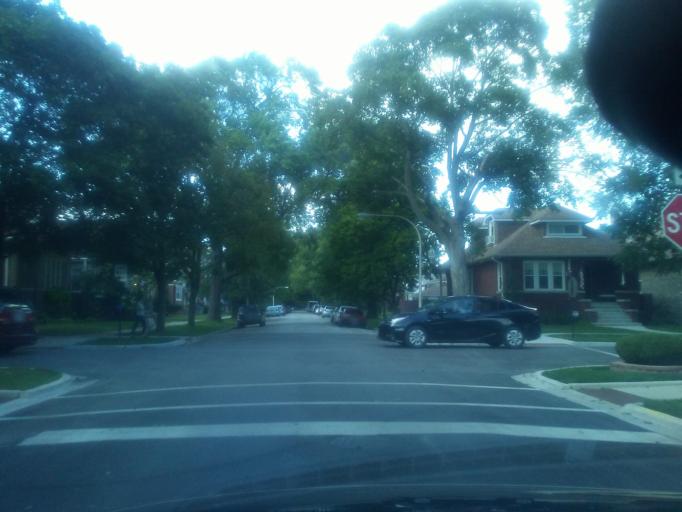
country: US
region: Illinois
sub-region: Cook County
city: Lincolnwood
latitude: 41.9717
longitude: -87.7331
